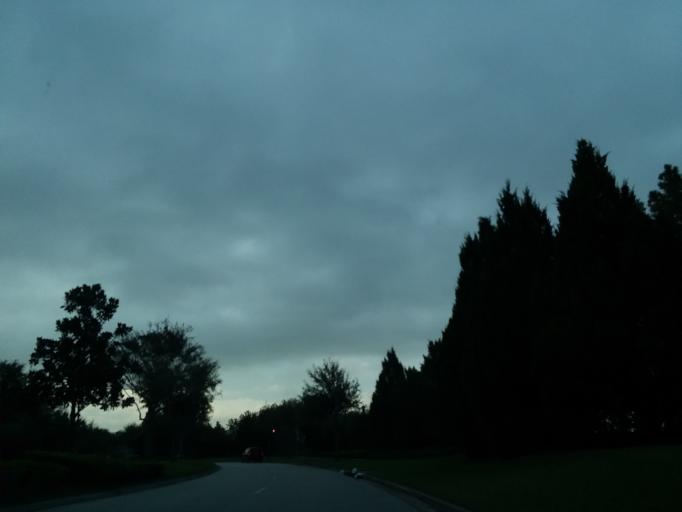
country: US
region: Florida
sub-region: Osceola County
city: Poinciana
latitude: 28.1818
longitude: -81.4371
